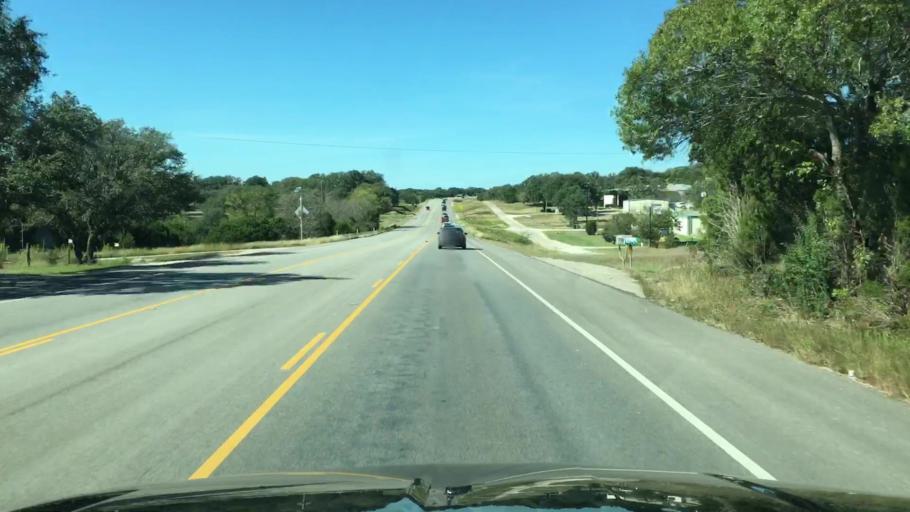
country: US
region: Texas
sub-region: Hays County
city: Dripping Springs
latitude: 30.1976
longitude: -98.1682
